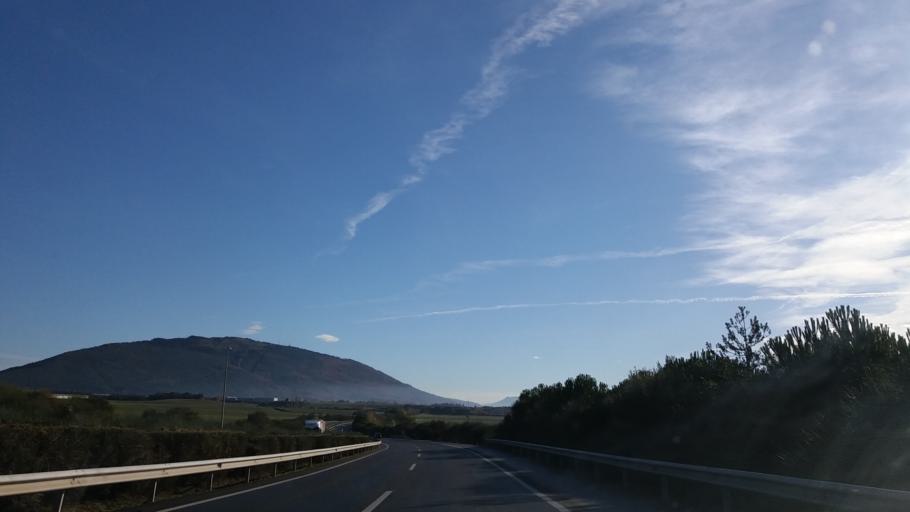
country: ES
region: Navarre
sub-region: Provincia de Navarra
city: Berriobeiti
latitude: 42.8553
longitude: -1.7281
